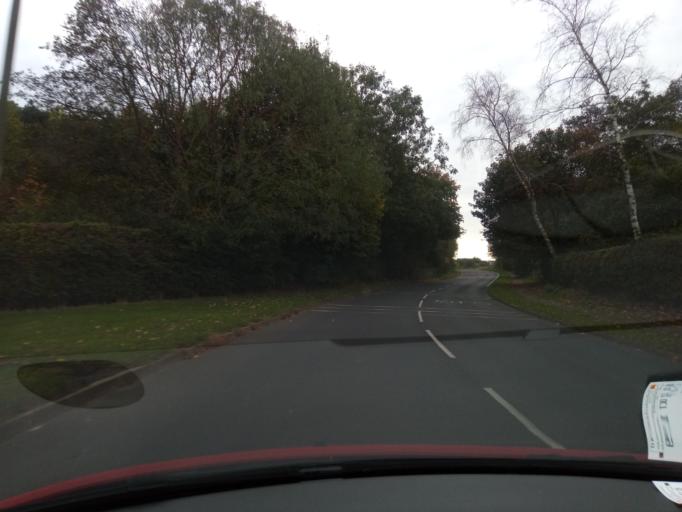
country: GB
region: England
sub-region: County Durham
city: Bishop Auckland
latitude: 54.6451
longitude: -1.6584
